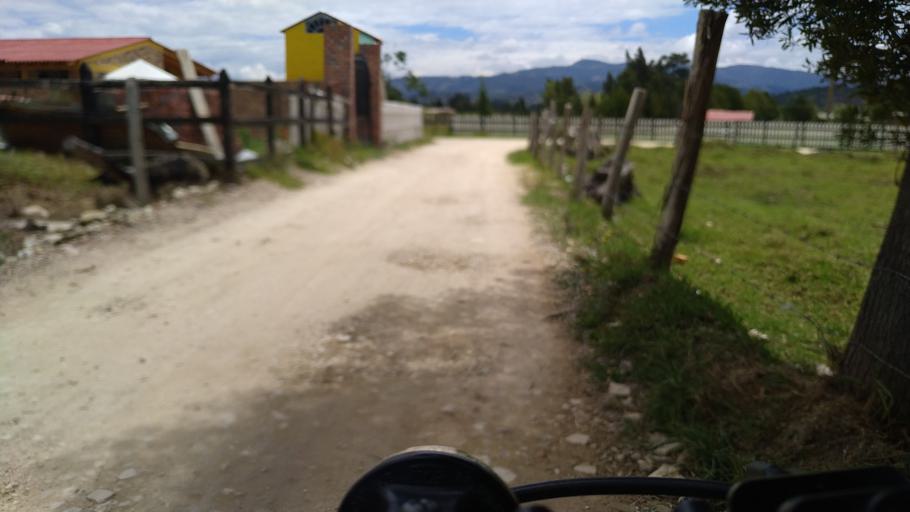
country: CO
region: Boyaca
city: Paipa
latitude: 5.7835
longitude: -73.0847
